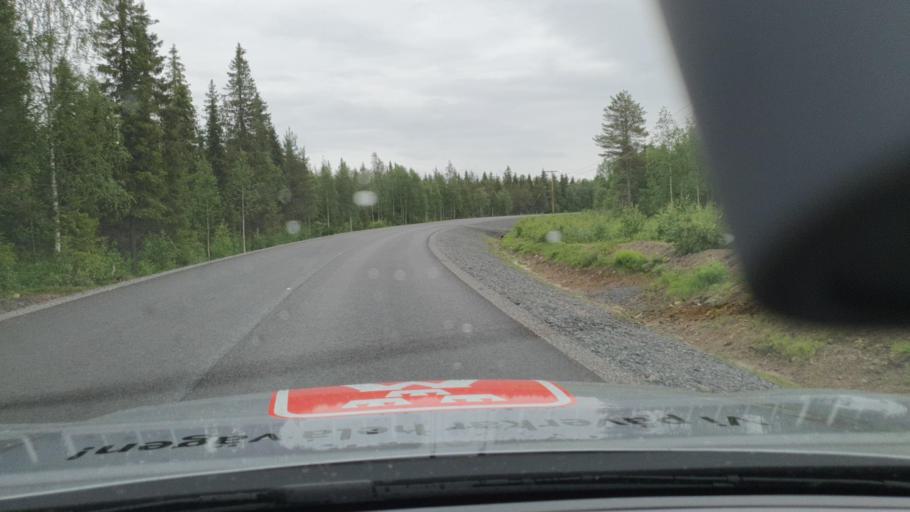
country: SE
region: Norrbotten
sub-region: Overkalix Kommun
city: OEverkalix
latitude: 66.7109
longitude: 23.2043
